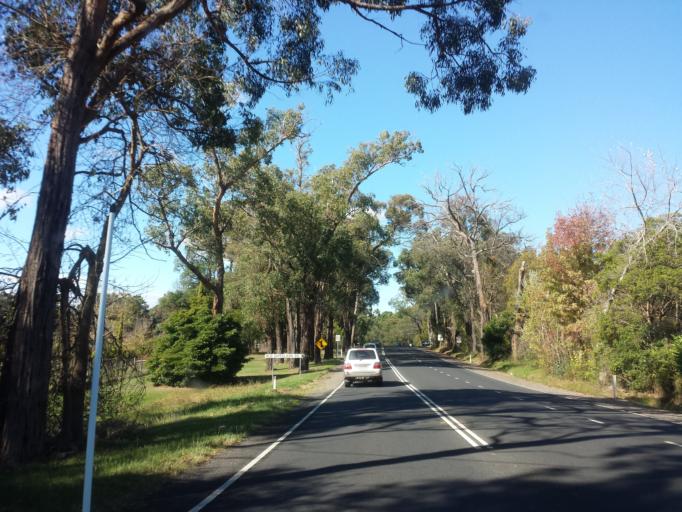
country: AU
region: Victoria
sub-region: Yarra Ranges
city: Mount Evelyn
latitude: -37.7655
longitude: 145.4025
